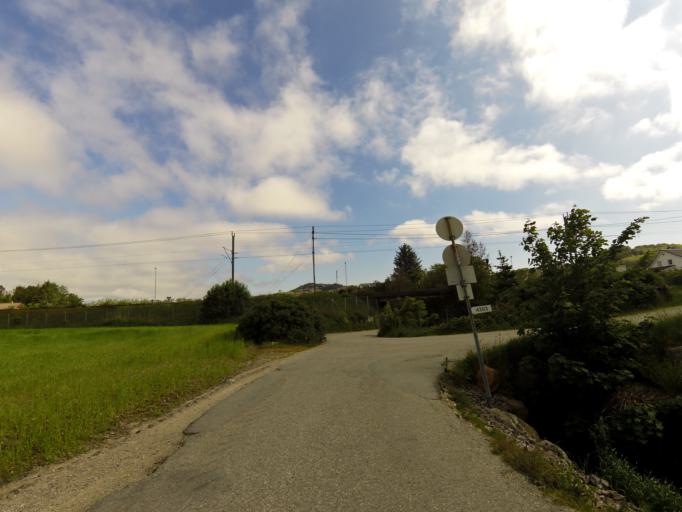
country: NO
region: Rogaland
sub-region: Ha
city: Vigrestad
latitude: 58.5209
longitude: 5.7995
